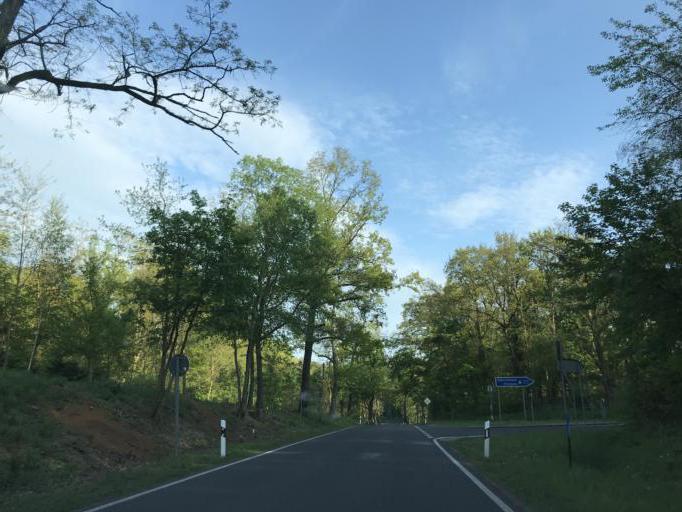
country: DE
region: Brandenburg
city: Joachimsthal
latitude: 52.8915
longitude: 13.7194
